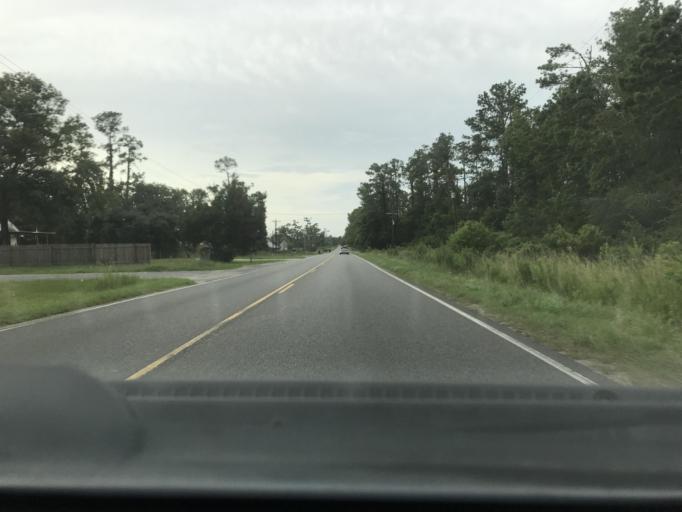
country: US
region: Louisiana
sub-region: Calcasieu Parish
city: Westlake
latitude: 30.2879
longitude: -93.2498
